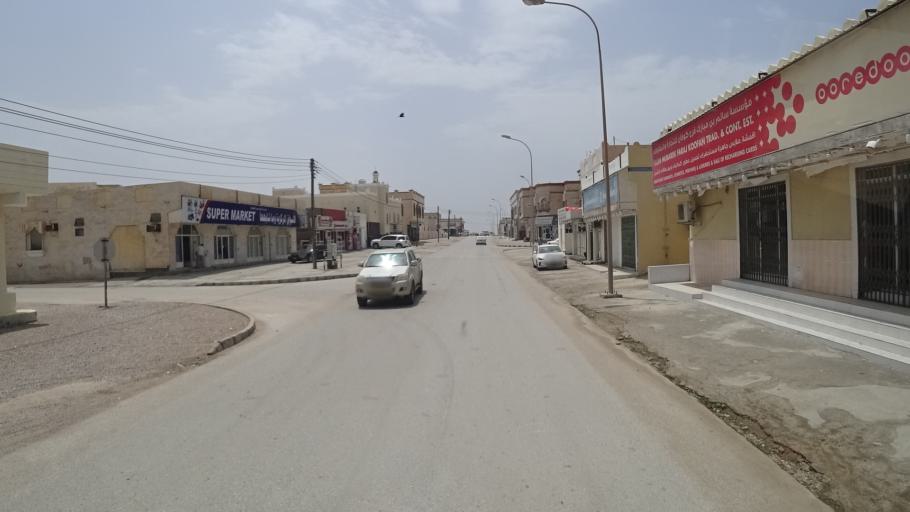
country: OM
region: Zufar
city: Salalah
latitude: 16.9828
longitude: 54.6904
